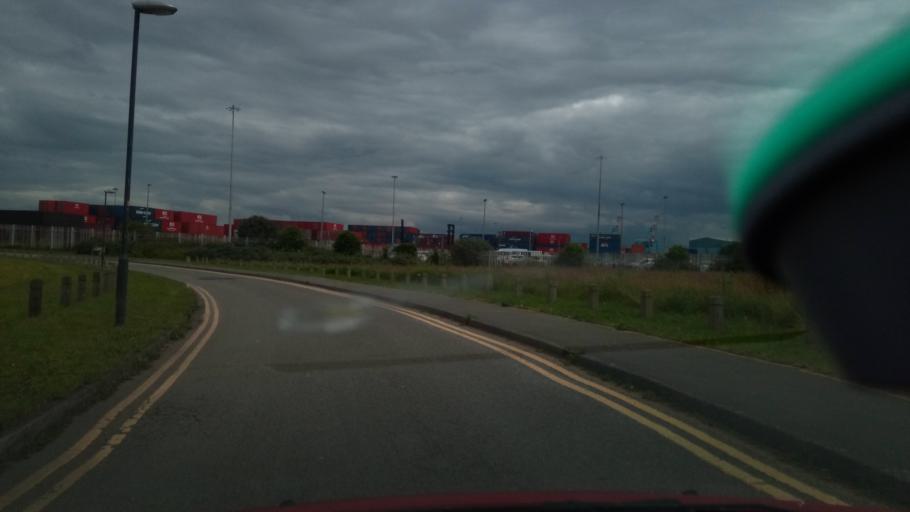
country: GB
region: England
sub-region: Sefton
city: Waterloo
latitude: 53.4687
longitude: -3.0260
